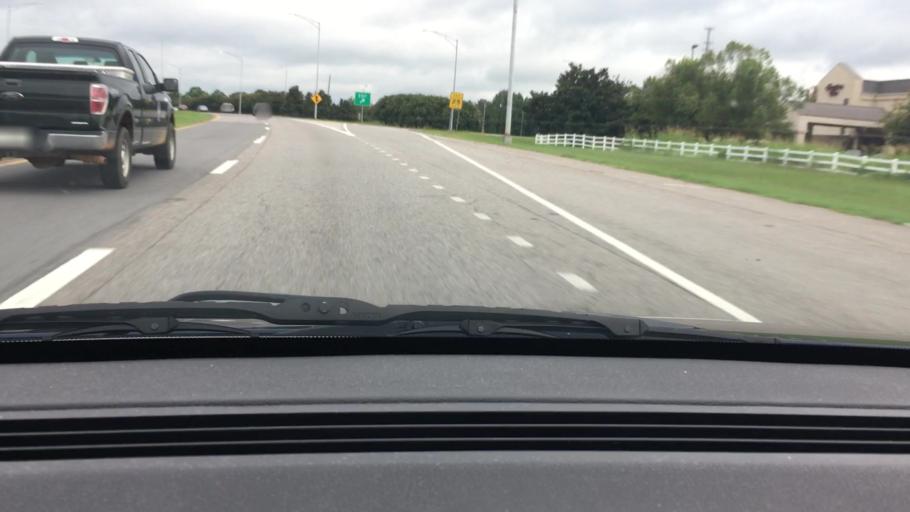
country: US
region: Alabama
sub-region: Tuscaloosa County
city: Tuscaloosa
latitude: 33.2109
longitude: -87.5247
